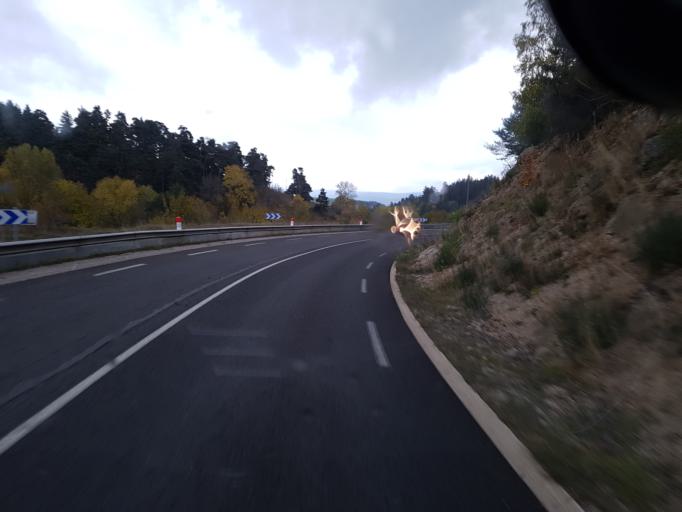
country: FR
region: Languedoc-Roussillon
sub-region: Departement de la Lozere
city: Mende
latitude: 44.5623
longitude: 3.6229
